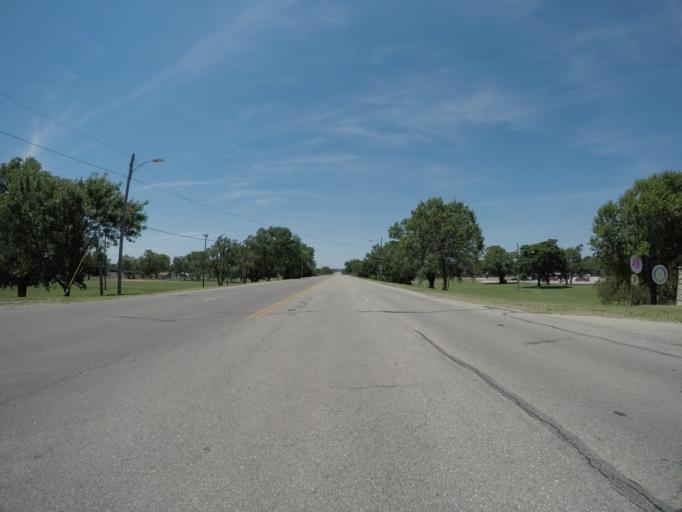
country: US
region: Kansas
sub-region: Geary County
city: Junction City
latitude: 39.0283
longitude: -96.8139
